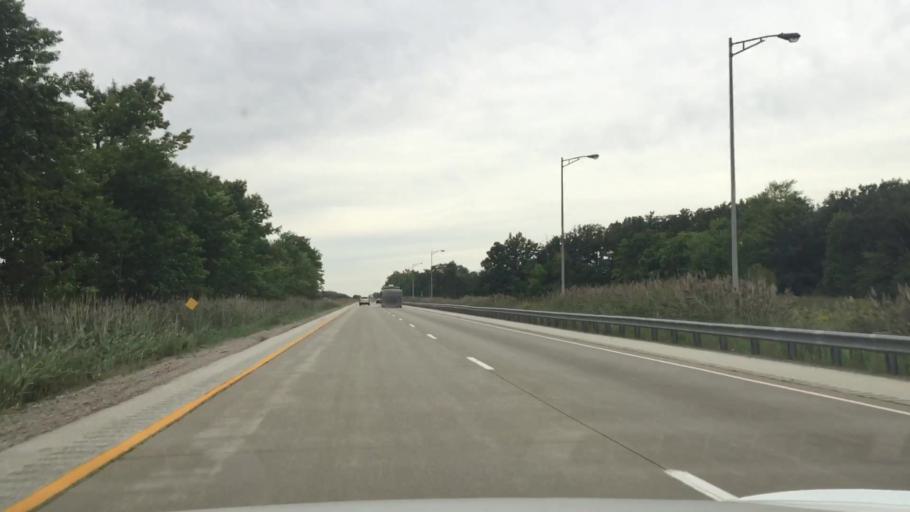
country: CA
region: Ontario
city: Camlachie
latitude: 42.9924
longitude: -82.1712
